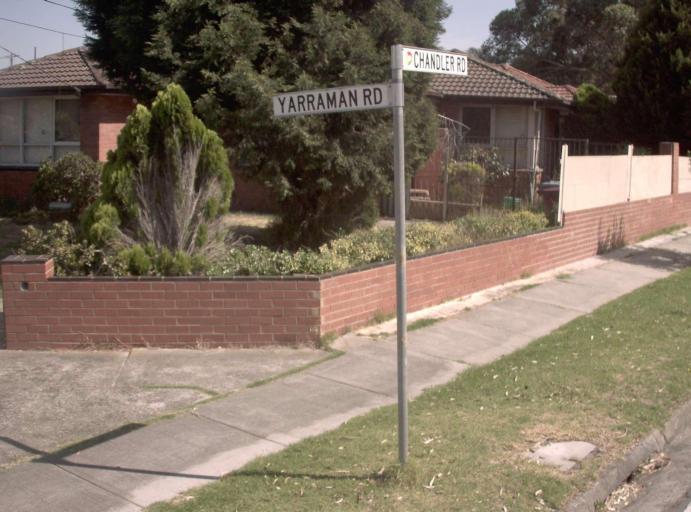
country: AU
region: Victoria
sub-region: Greater Dandenong
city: Dandenong
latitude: -37.9774
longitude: 145.1851
